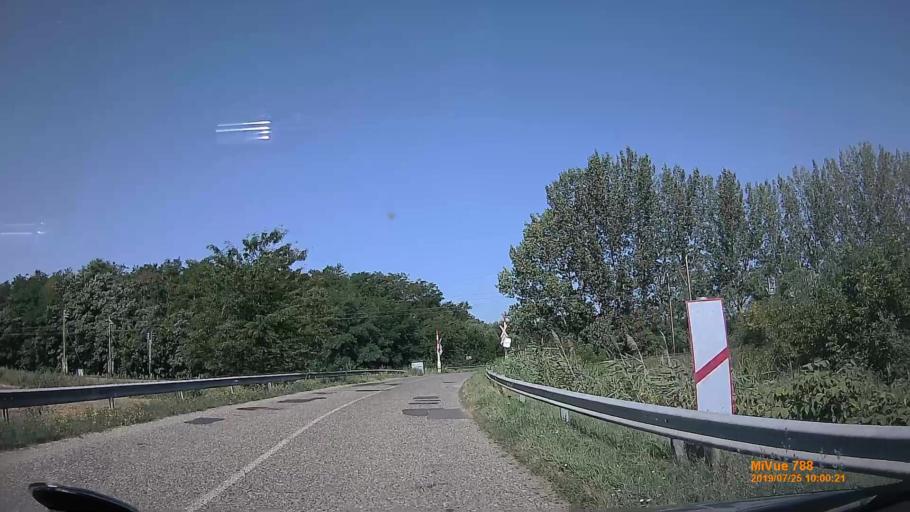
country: HU
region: Szabolcs-Szatmar-Bereg
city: Kotaj
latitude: 48.0293
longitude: 21.7580
